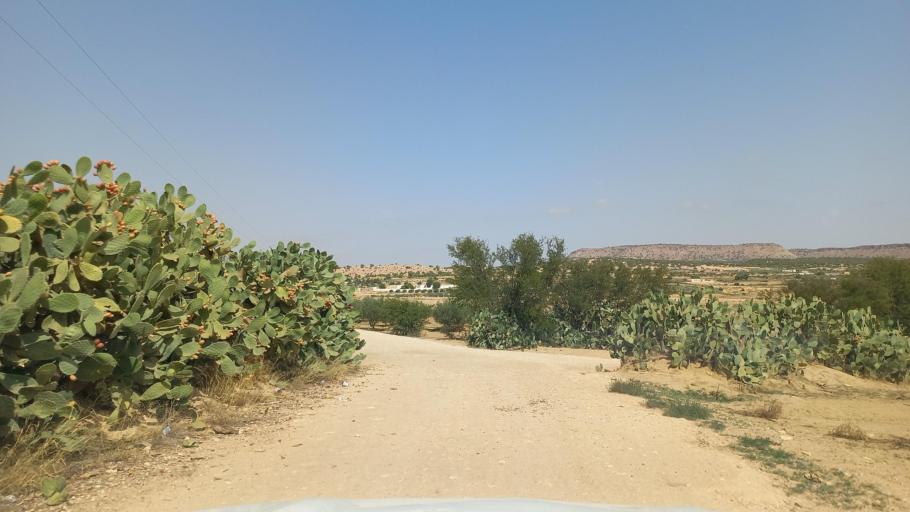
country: TN
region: Al Qasrayn
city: Sbiba
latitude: 35.3876
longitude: 8.9589
